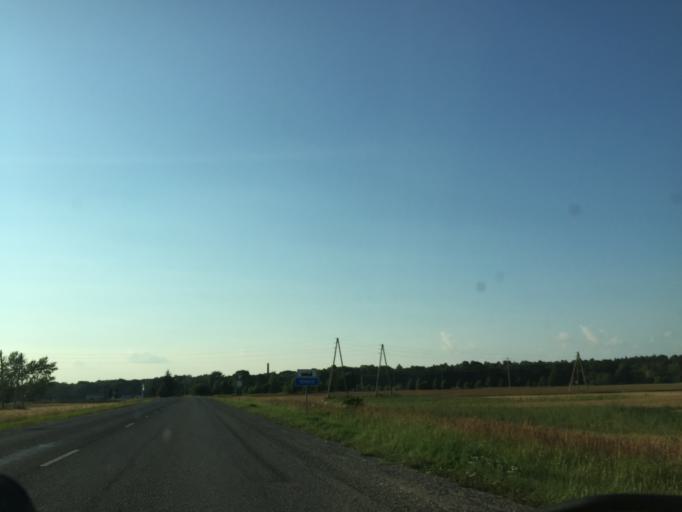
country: LV
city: Tervete
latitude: 56.4744
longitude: 23.3950
